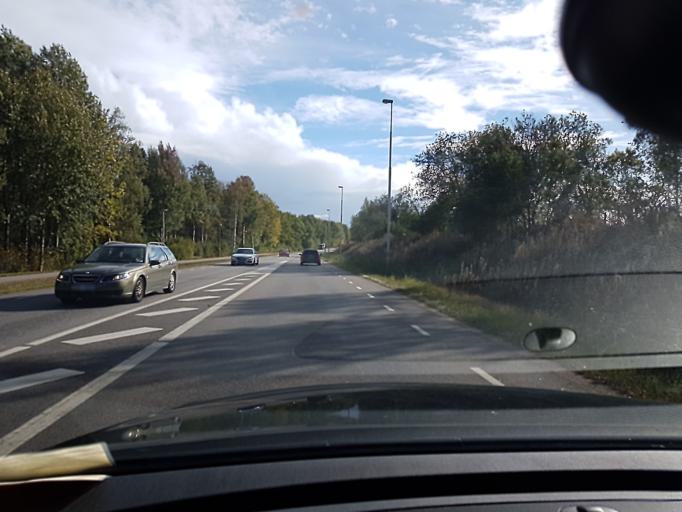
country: SE
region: Kronoberg
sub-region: Vaxjo Kommun
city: Vaexjoe
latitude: 56.8725
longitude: 14.7864
